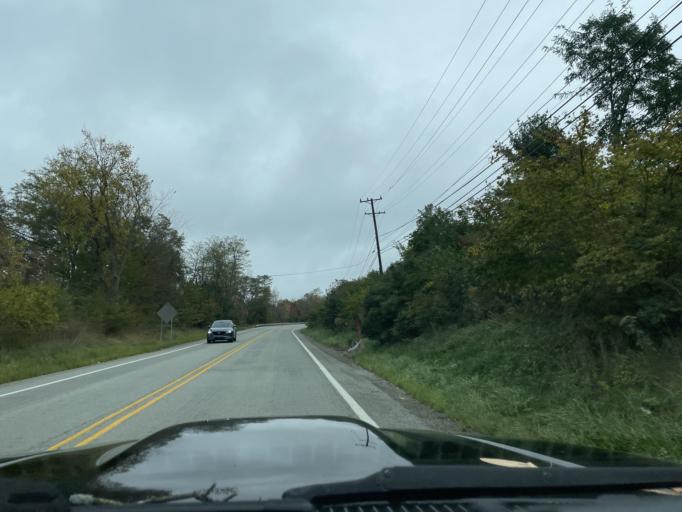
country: US
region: Pennsylvania
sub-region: Allegheny County
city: Cheswick
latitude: 40.5281
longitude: -79.8055
